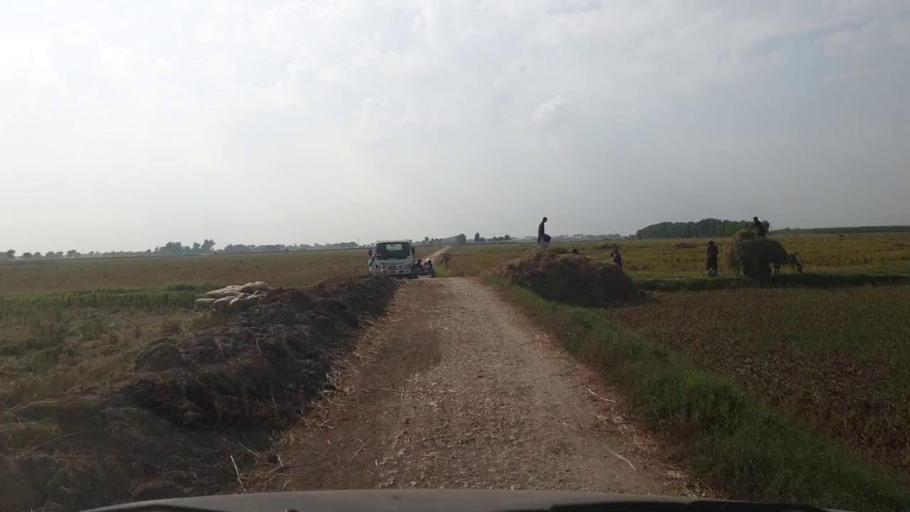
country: PK
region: Sindh
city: Kario
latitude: 24.6345
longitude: 68.5544
